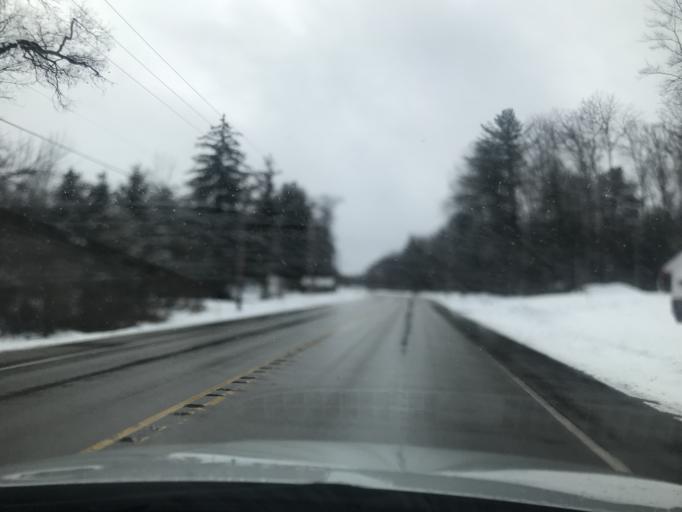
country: US
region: Wisconsin
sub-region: Marinette County
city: Peshtigo
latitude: 45.1710
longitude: -87.7366
